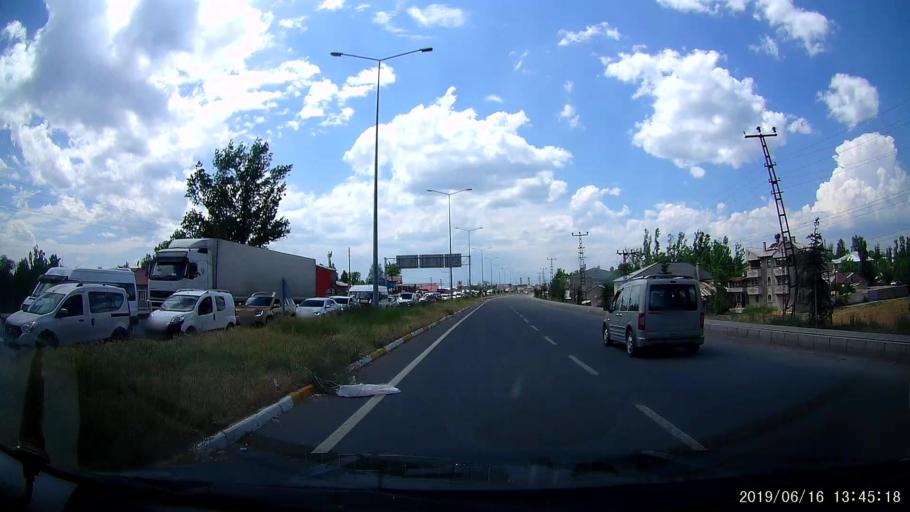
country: TR
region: Agri
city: Agri
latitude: 39.7084
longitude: 43.0473
